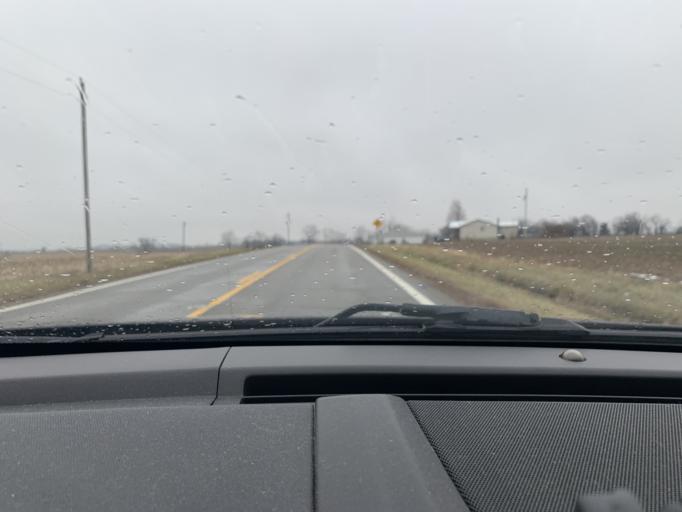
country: US
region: Ohio
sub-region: Ross County
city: Kingston
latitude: 39.4380
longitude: -82.8794
